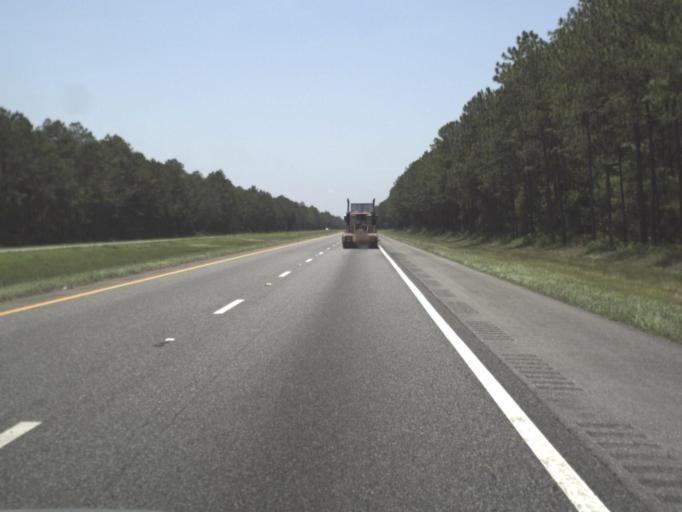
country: US
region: Florida
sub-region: Union County
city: Lake Butler
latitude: 30.2544
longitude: -82.3601
